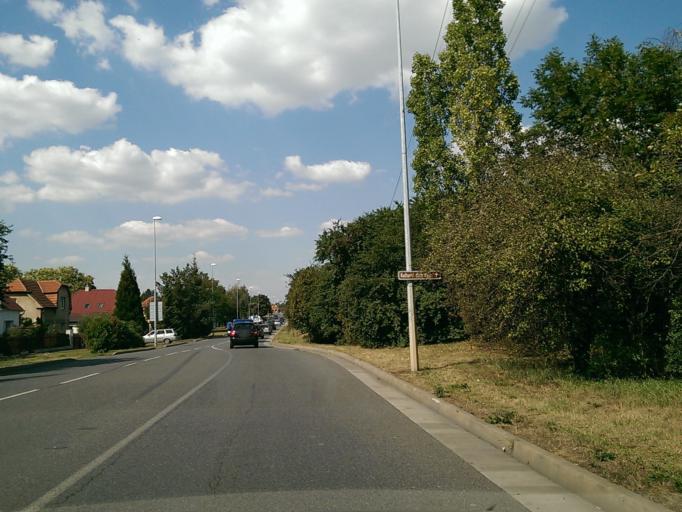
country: CZ
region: Praha
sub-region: Praha 14
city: Hostavice
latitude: 50.0901
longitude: 14.5472
